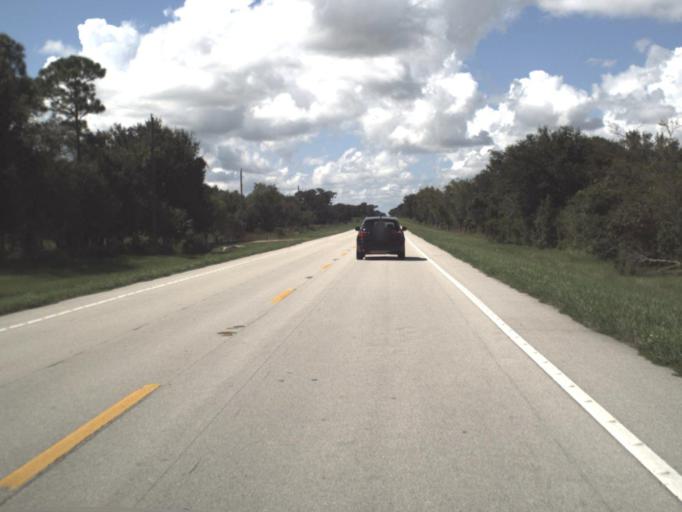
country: US
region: Florida
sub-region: DeSoto County
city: Arcadia
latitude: 27.2683
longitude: -81.9991
